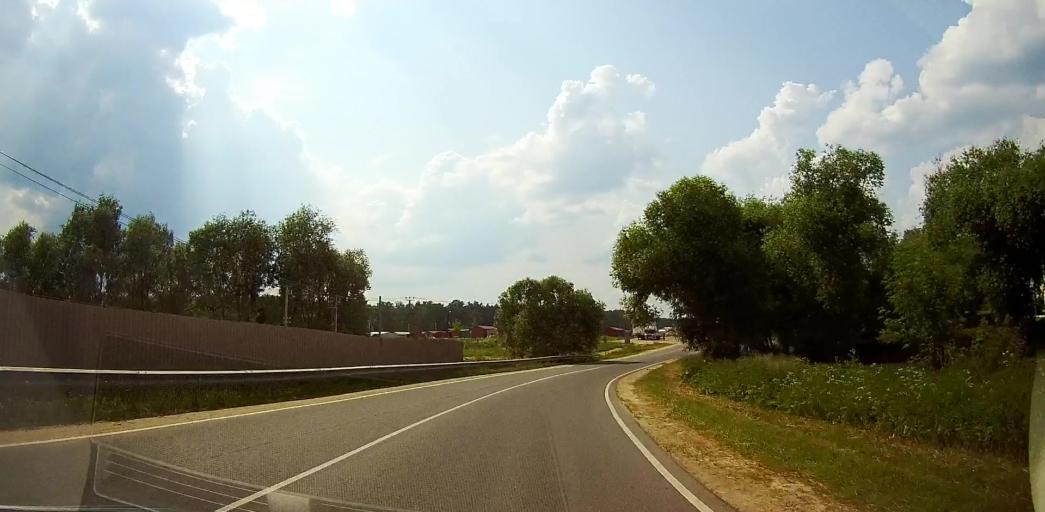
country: RU
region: Moskovskaya
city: Zhilevo
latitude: 55.0517
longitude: 37.9880
